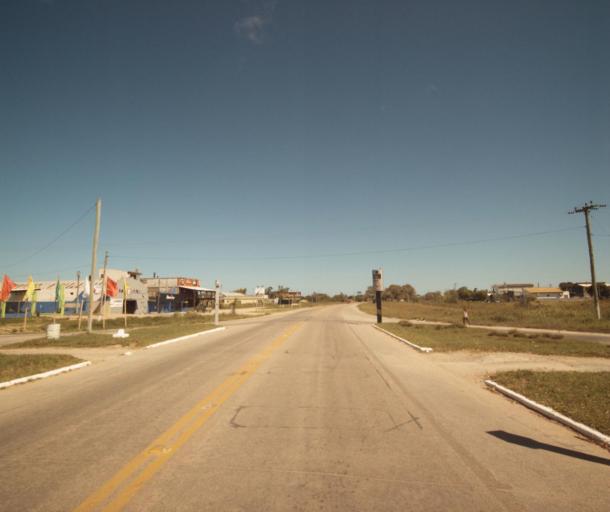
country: BR
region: Rio Grande do Sul
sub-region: Chui
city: Chui
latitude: -33.6895
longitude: -53.4472
